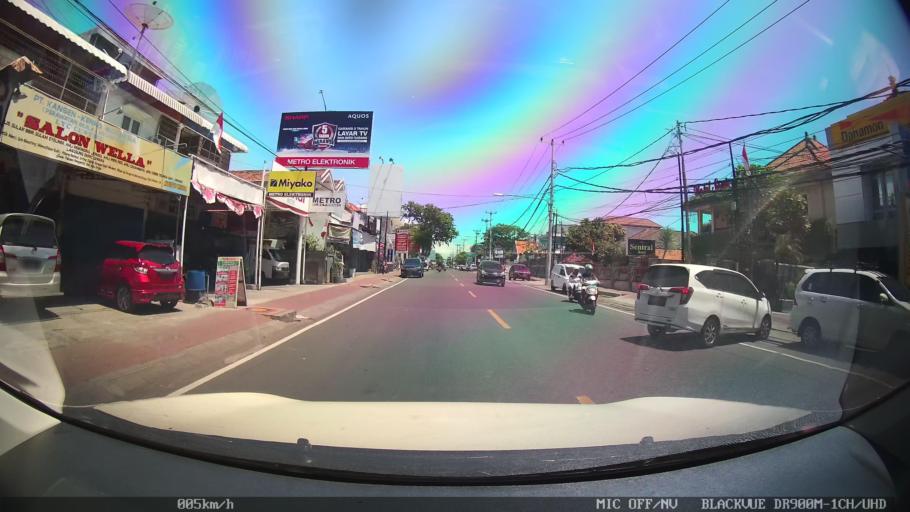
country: ID
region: Bali
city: Singaraja
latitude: -8.1106
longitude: 115.0879
